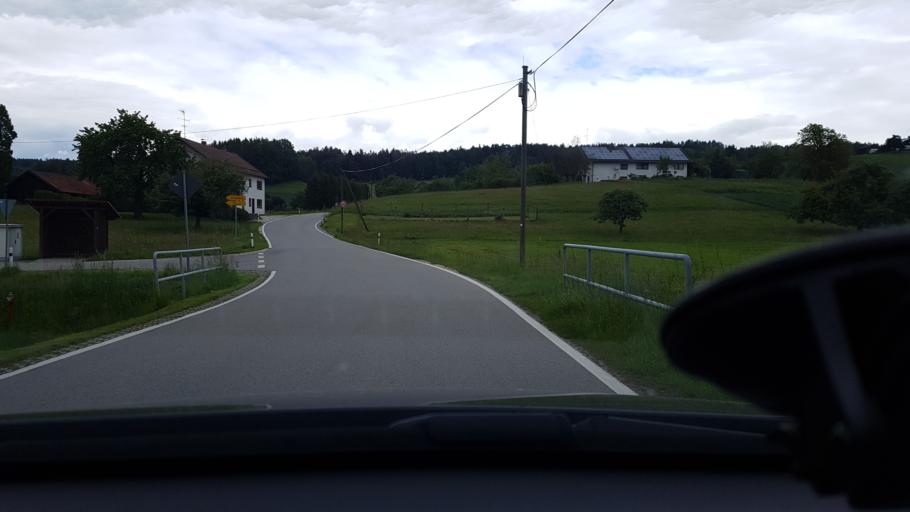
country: DE
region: Bavaria
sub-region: Lower Bavaria
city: Stubenberg
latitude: 48.3145
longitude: 13.0694
